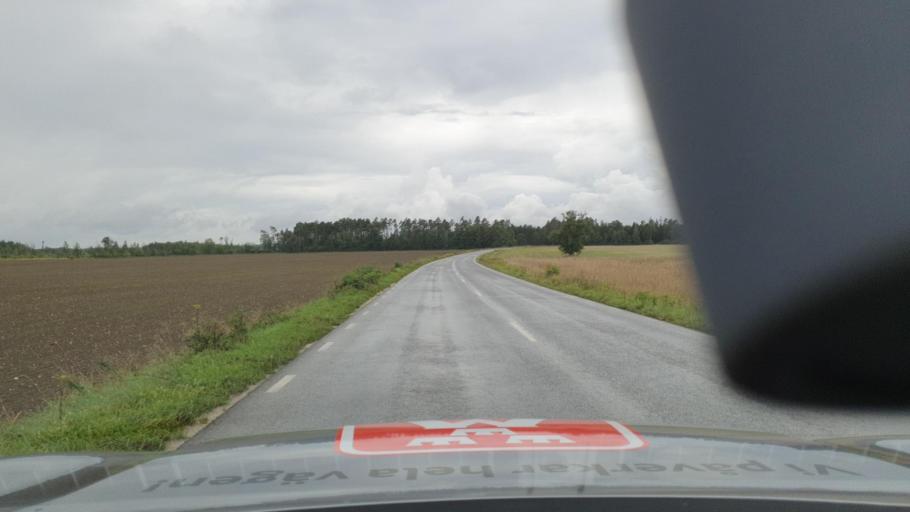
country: SE
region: Gotland
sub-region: Gotland
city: Visby
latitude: 57.5005
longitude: 18.3966
